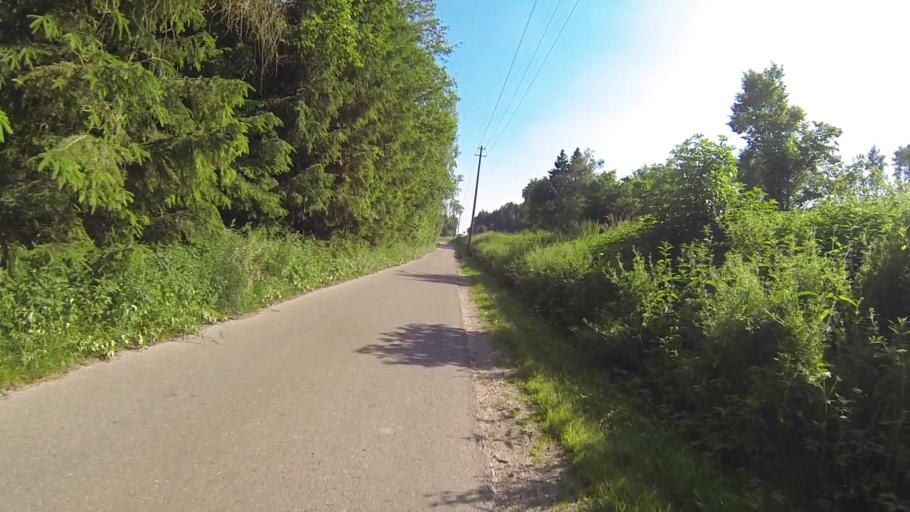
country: DE
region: Baden-Wuerttemberg
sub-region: Tuebingen Region
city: Warthausen
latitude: 48.1851
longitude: 9.8273
